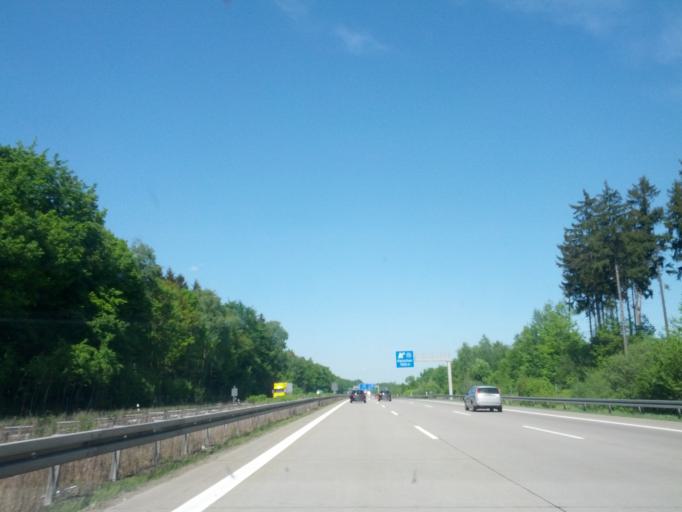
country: DE
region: Saxony
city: Rossau
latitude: 50.9736
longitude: 13.0867
